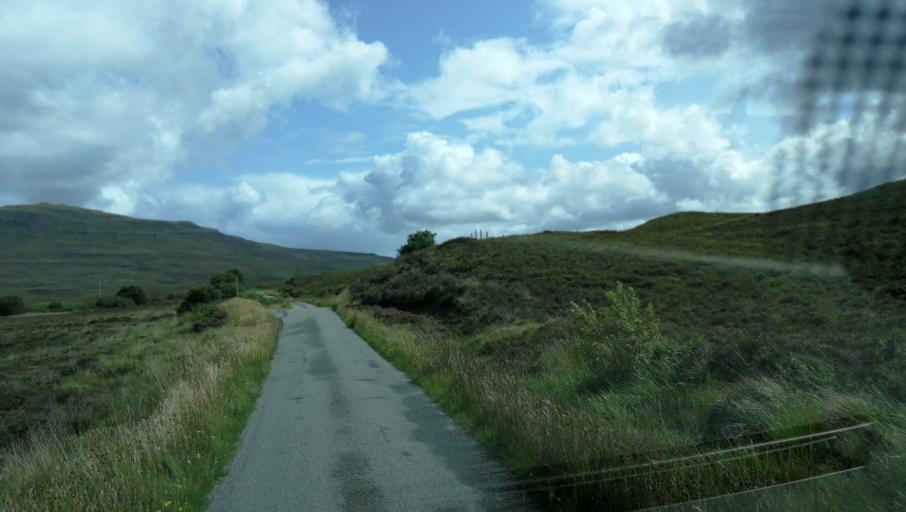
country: GB
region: Scotland
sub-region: Highland
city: Portree
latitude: 57.3848
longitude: -6.1904
